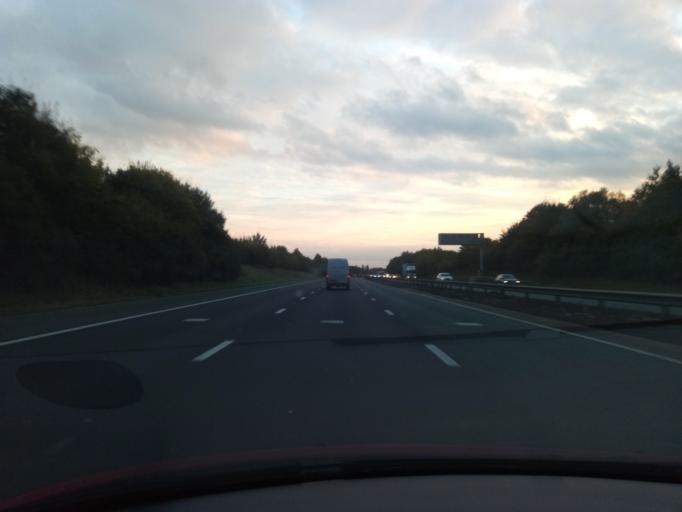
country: GB
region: England
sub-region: City and Borough of Leeds
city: Wetherby
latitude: 53.9885
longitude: -1.3629
